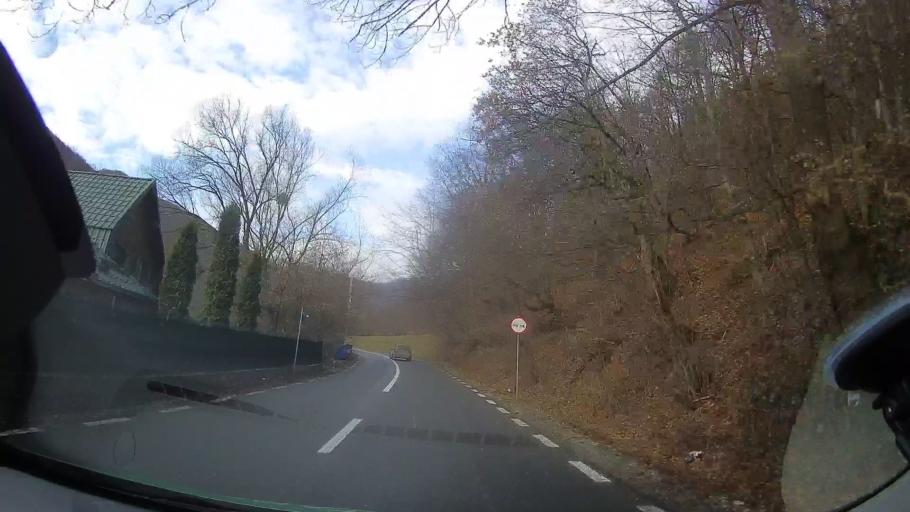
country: RO
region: Cluj
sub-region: Comuna Baisoara
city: Baisoara
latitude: 46.6101
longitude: 23.4155
